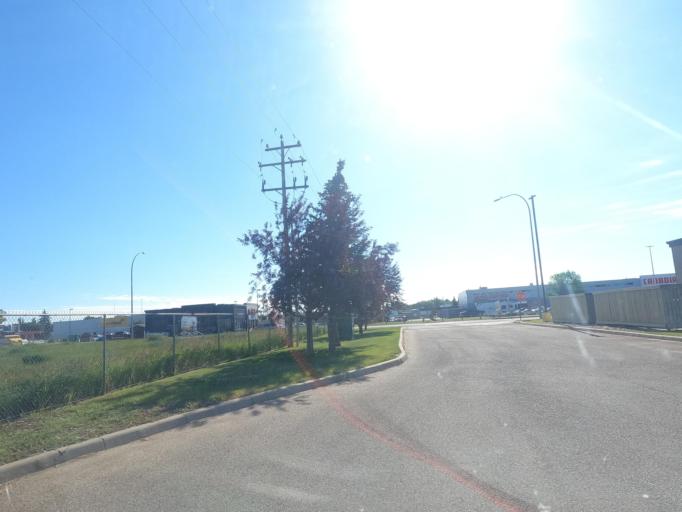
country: CA
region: Alberta
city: Brooks
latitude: 50.5735
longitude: -111.9016
